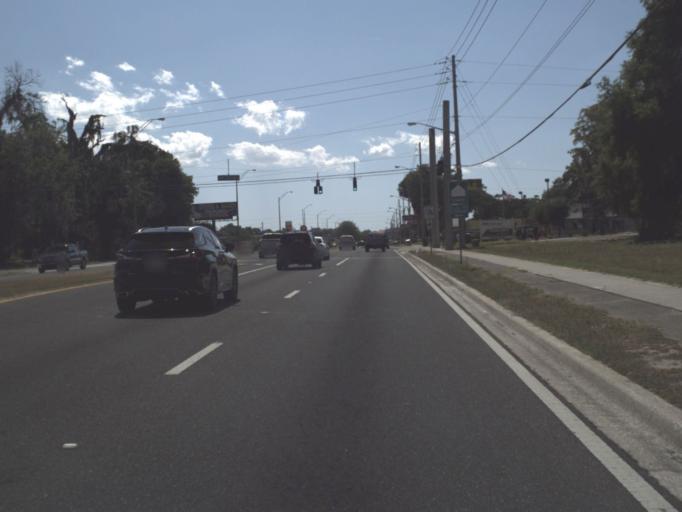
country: US
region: Florida
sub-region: Marion County
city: Ocala
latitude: 29.1864
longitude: -82.1762
